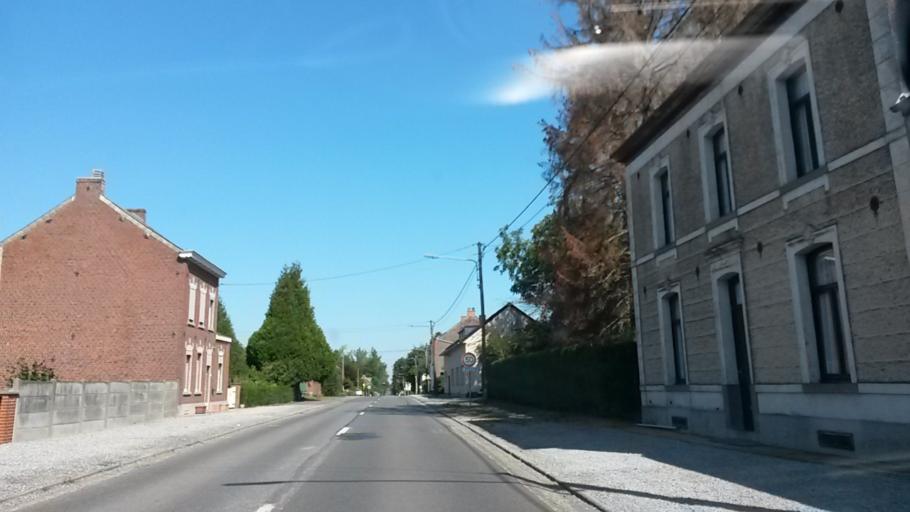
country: BE
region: Wallonia
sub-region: Province du Hainaut
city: Merbes-le-Chateau
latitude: 50.3618
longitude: 4.1757
